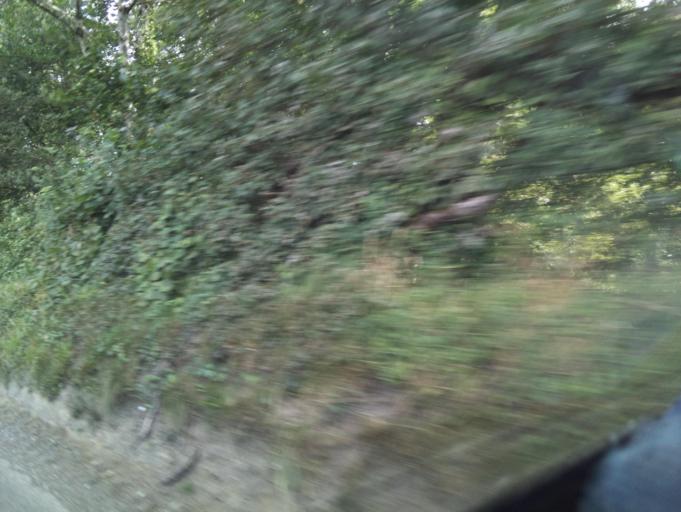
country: GB
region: England
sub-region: Somerset
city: Redlynch
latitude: 51.0956
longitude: -2.4198
